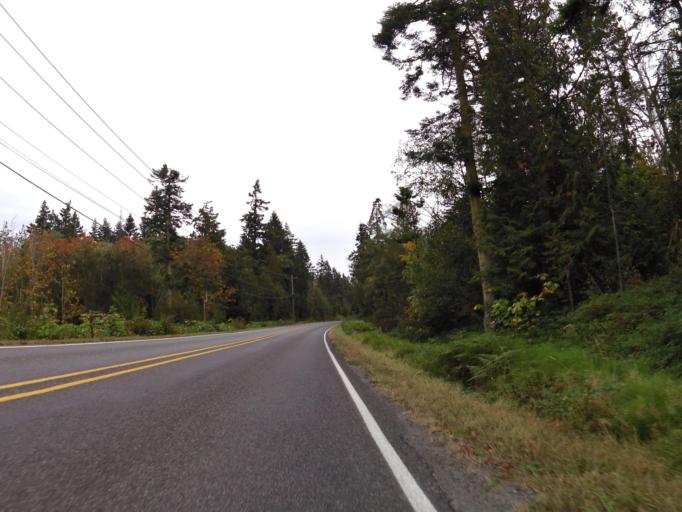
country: US
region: Washington
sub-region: Jefferson County
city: Port Hadlock-Irondale
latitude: 48.0232
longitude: -122.7386
